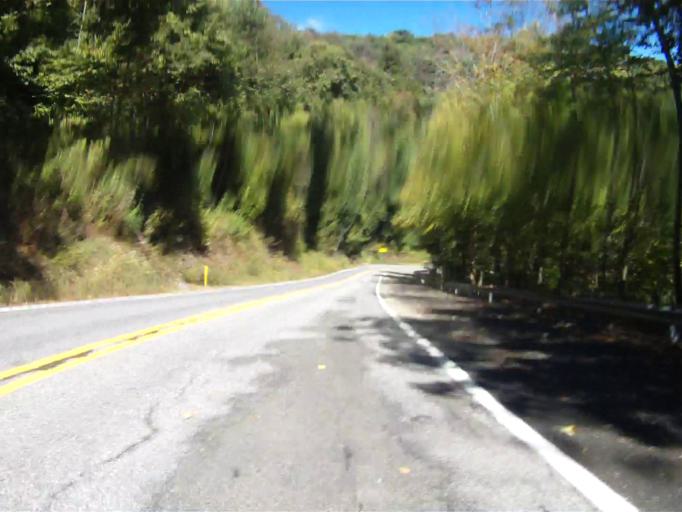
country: US
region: Pennsylvania
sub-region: Centre County
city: Park Forest Village
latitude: 40.9255
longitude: -77.9470
